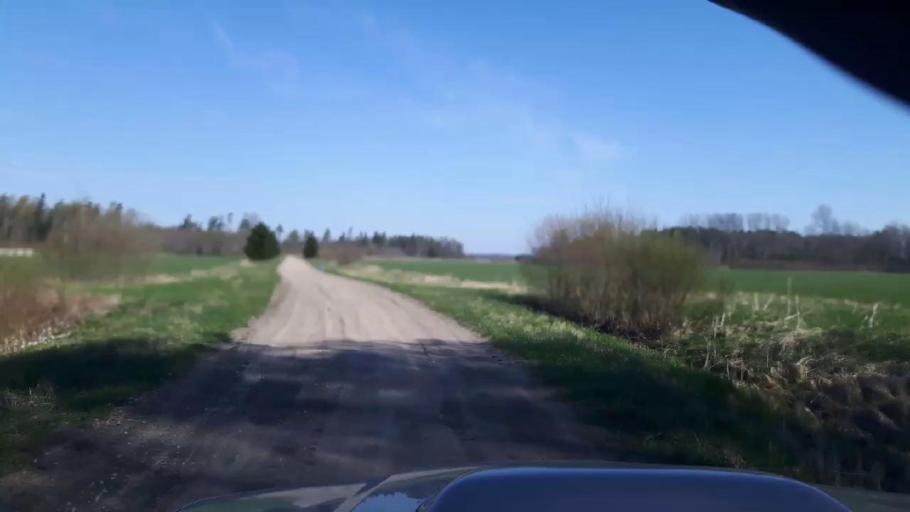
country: EE
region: Paernumaa
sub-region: Vaendra vald (alev)
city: Vandra
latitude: 58.5206
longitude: 24.9607
